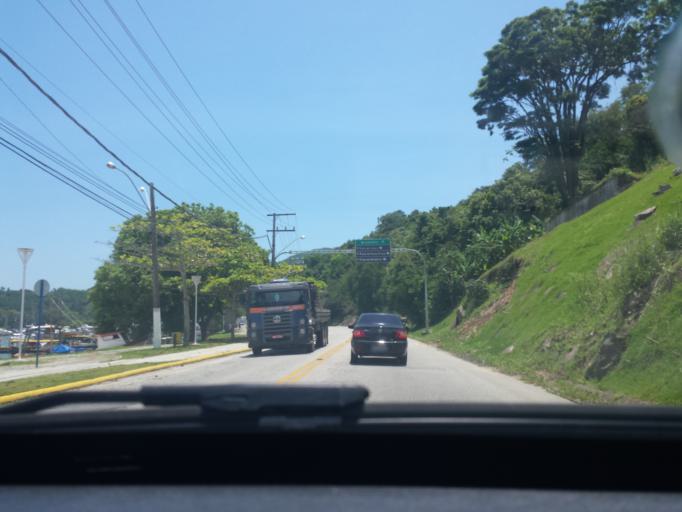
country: BR
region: Santa Catarina
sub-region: Porto Belo
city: Porto Belo
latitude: -27.1498
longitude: -48.5360
